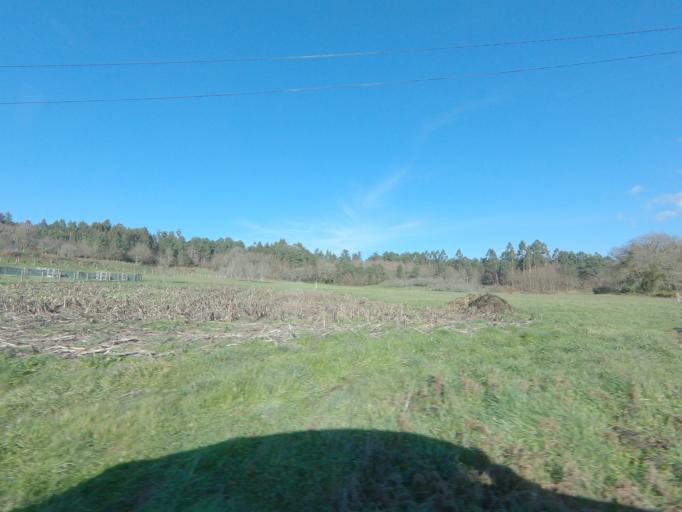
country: ES
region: Galicia
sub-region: Provincia da Coruna
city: Ribeira
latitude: 42.7139
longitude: -8.4350
